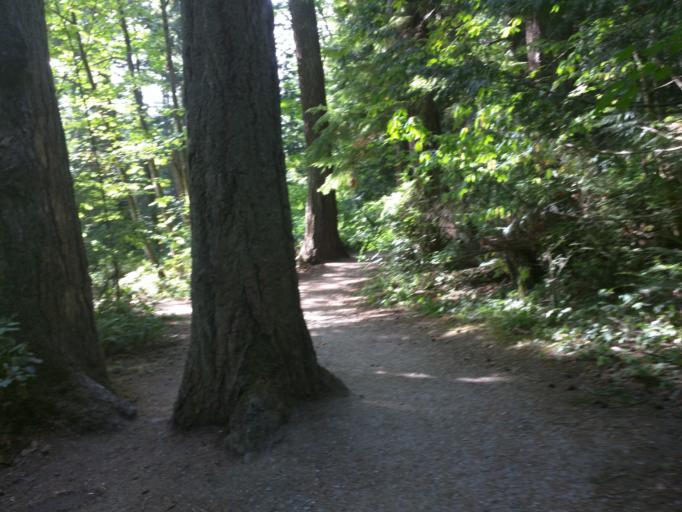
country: US
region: Washington
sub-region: Whatcom County
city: Geneva
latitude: 48.7522
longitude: -122.4329
